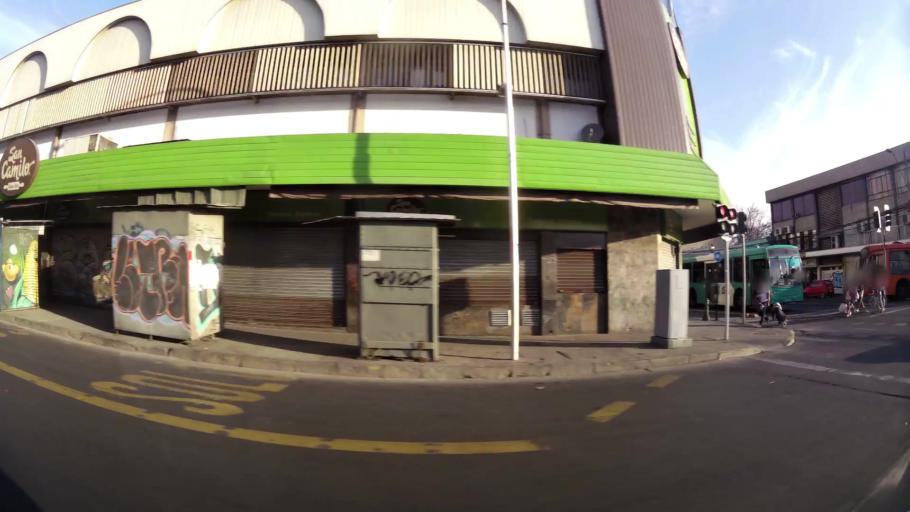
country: CL
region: Santiago Metropolitan
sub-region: Provincia de Santiago
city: Santiago
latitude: -33.4359
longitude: -70.6801
